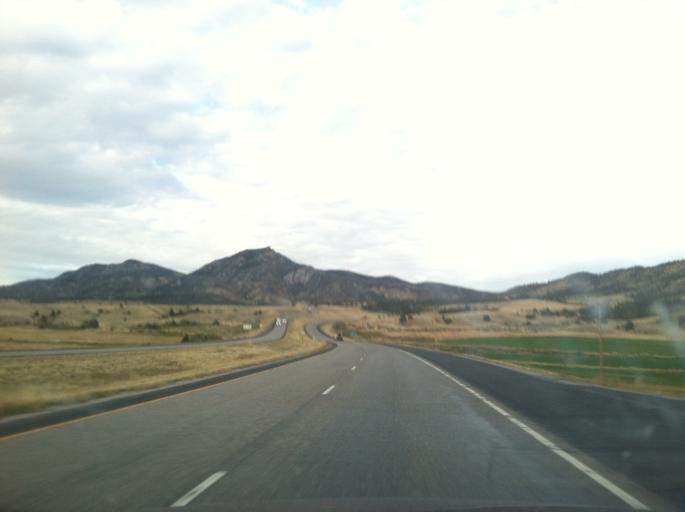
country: US
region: Montana
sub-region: Jefferson County
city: Whitehall
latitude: 45.8710
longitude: -111.9394
